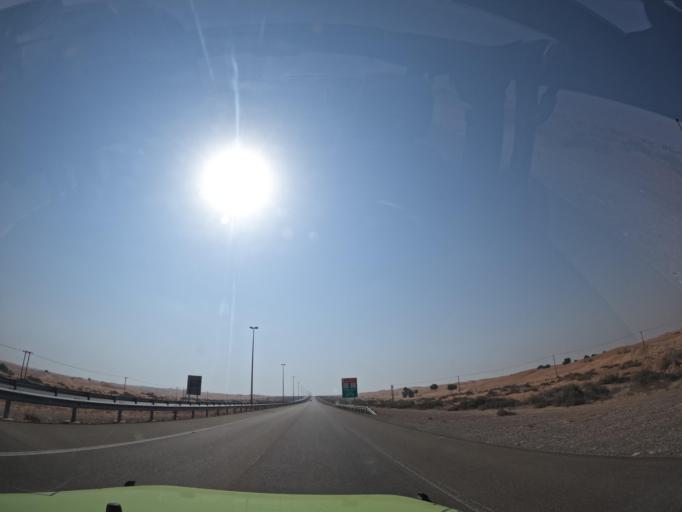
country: OM
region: Al Buraimi
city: Al Buraymi
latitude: 24.4552
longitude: 55.6472
